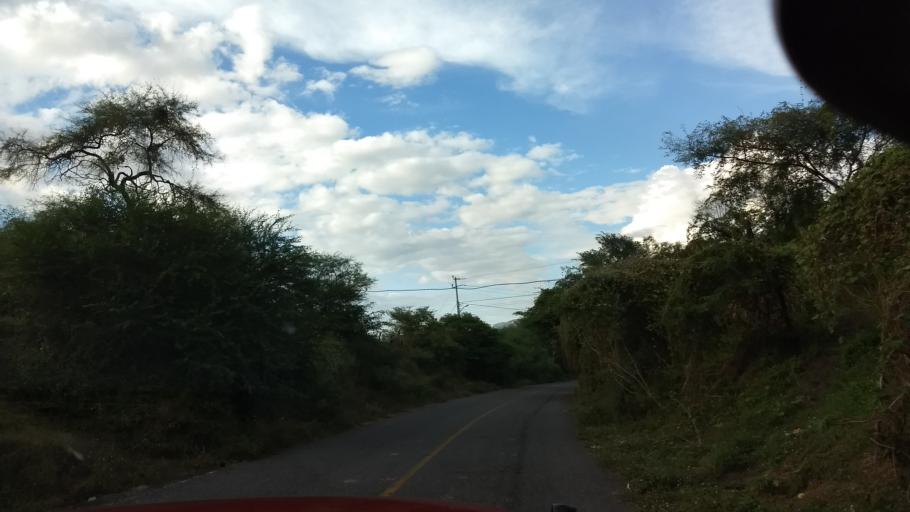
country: MX
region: Colima
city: Suchitlan
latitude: 19.4565
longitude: -103.8264
